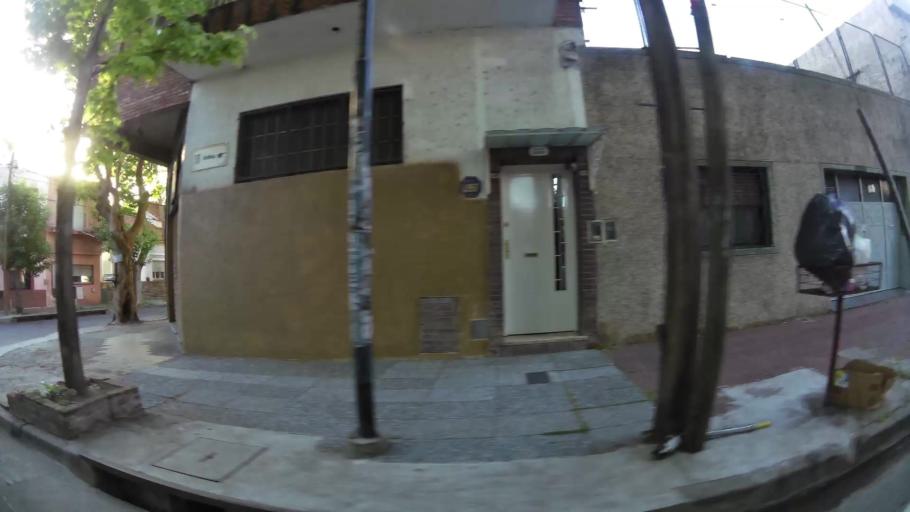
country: AR
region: Buenos Aires
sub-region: Partido de General San Martin
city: General San Martin
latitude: -34.5701
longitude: -58.5325
